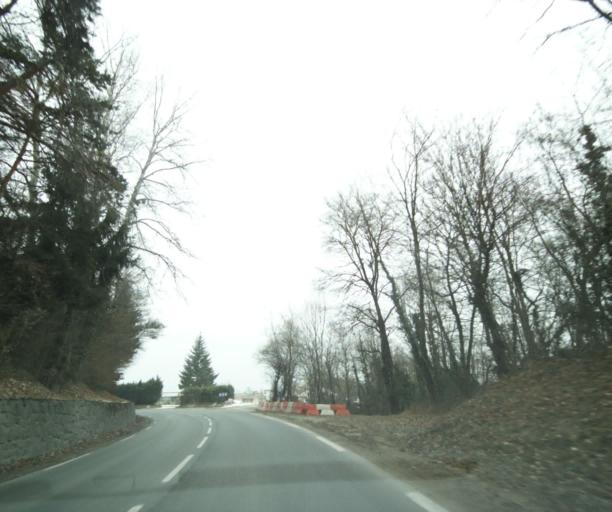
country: FR
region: Rhone-Alpes
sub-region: Departement de la Haute-Savoie
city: Arthaz-Pont-Notre-Dame
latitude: 46.1476
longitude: 6.2619
